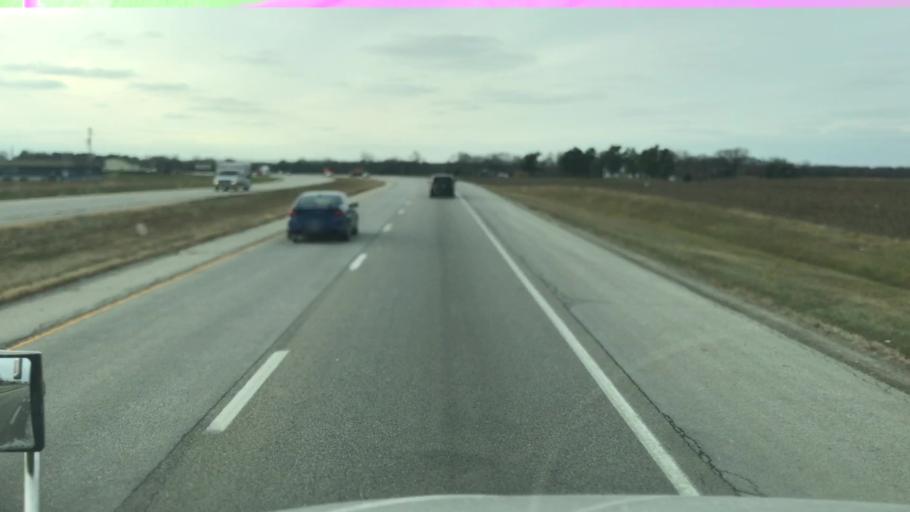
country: US
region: Illinois
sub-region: Warren County
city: Monmouth
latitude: 40.9257
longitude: -90.6509
